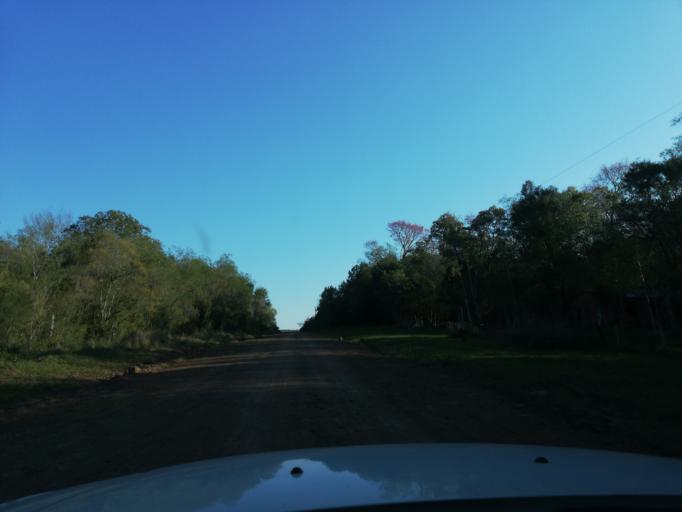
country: AR
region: Misiones
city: Cerro Cora
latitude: -27.5943
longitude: -55.6947
